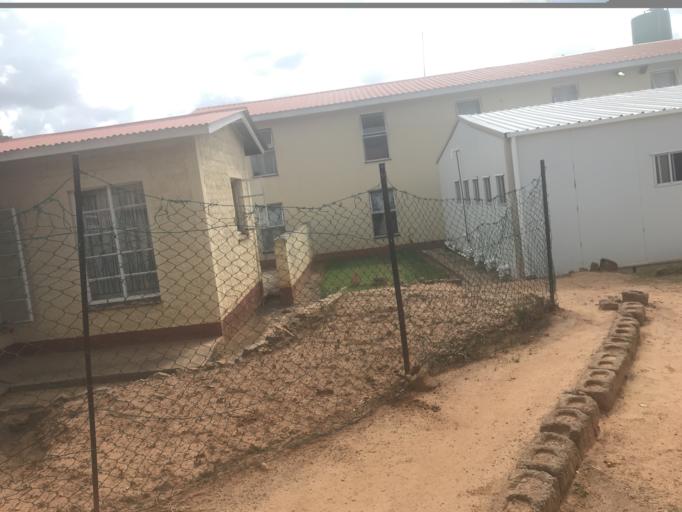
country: LS
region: Maseru
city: Nako
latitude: -29.6306
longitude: 27.5009
